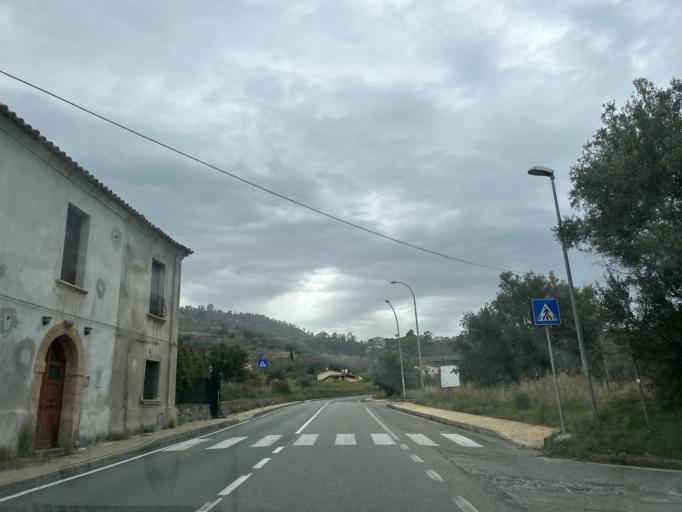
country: IT
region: Calabria
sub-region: Provincia di Catanzaro
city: Montepaone Lido
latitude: 38.7407
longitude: 16.5491
